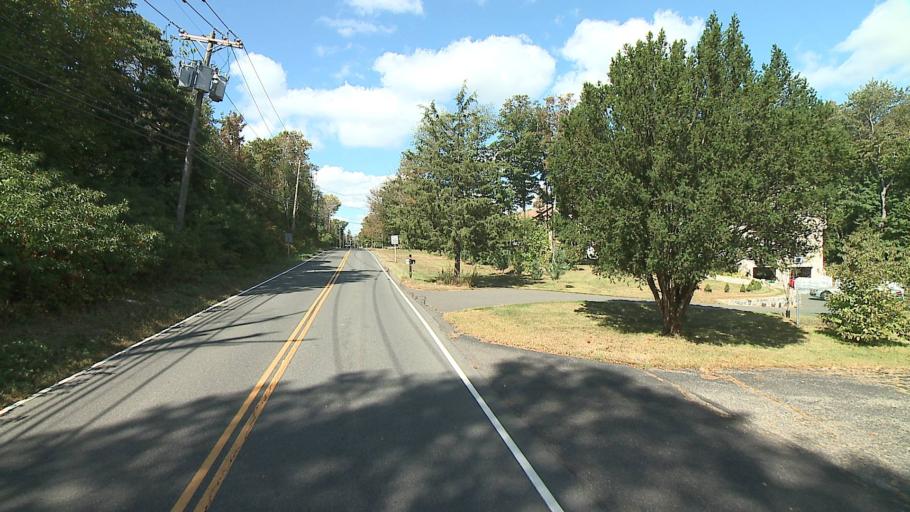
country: US
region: Connecticut
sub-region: New Haven County
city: Ansonia
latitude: 41.3608
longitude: -73.1146
